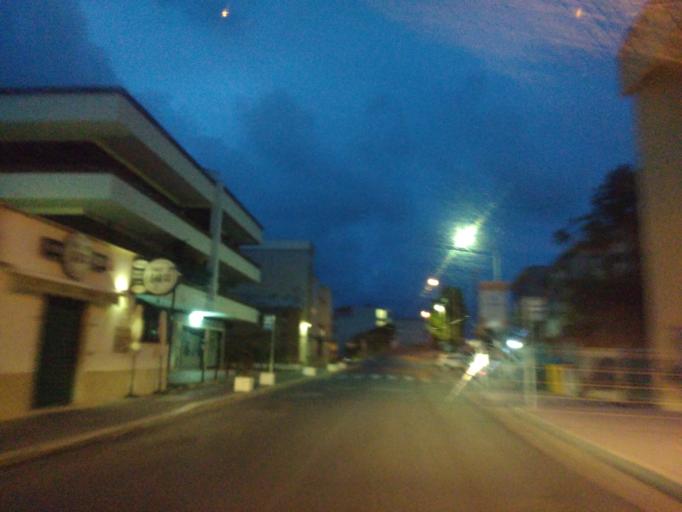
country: IT
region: Latium
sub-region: Citta metropolitana di Roma Capitale
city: Anzio
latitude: 41.4518
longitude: 12.6240
